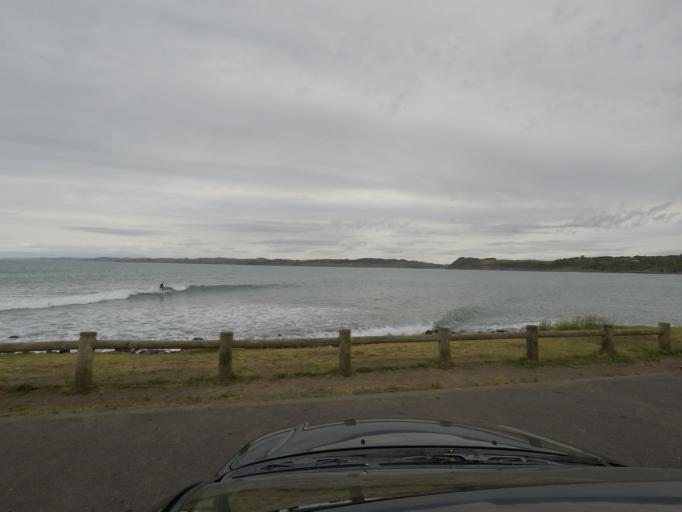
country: NZ
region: Waikato
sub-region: Waikato District
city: Raglan
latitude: -37.8214
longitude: 174.8128
